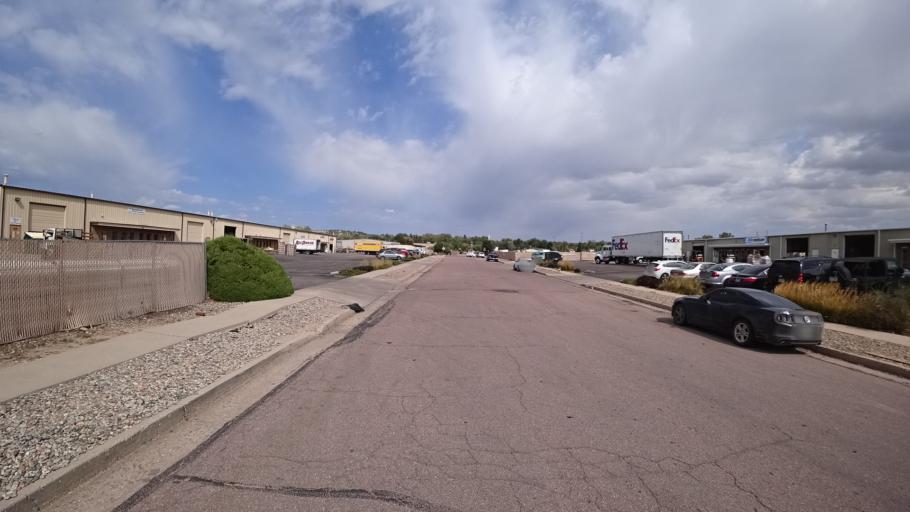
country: US
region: Colorado
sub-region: El Paso County
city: Cimarron Hills
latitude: 38.8429
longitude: -104.7338
